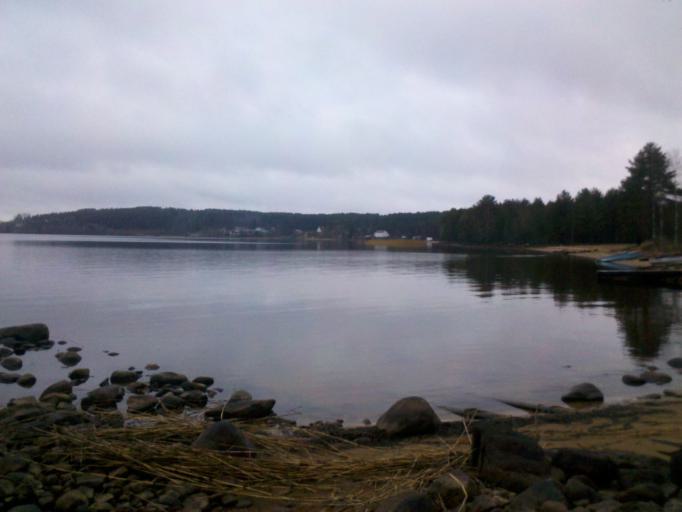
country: RU
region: Republic of Karelia
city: Essoyla
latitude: 61.9138
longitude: 33.3655
